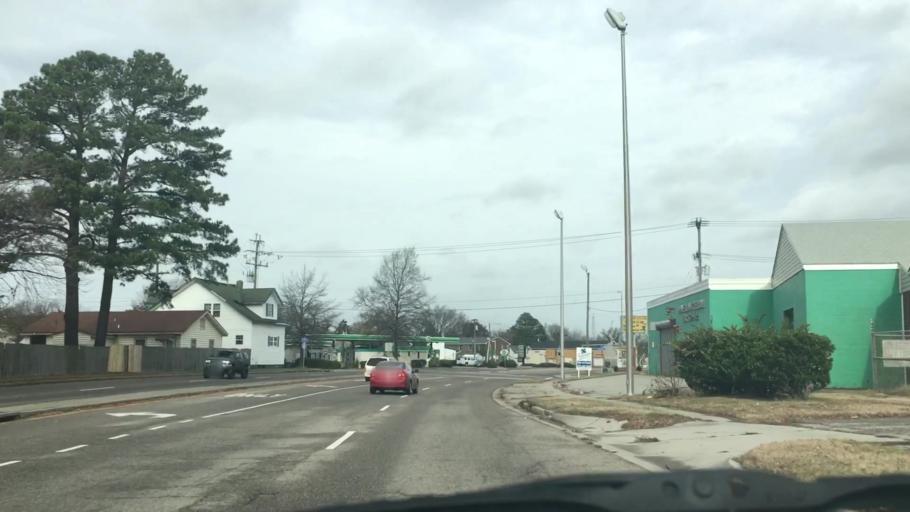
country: US
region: Virginia
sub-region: City of Norfolk
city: Norfolk
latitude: 36.8741
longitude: -76.2516
